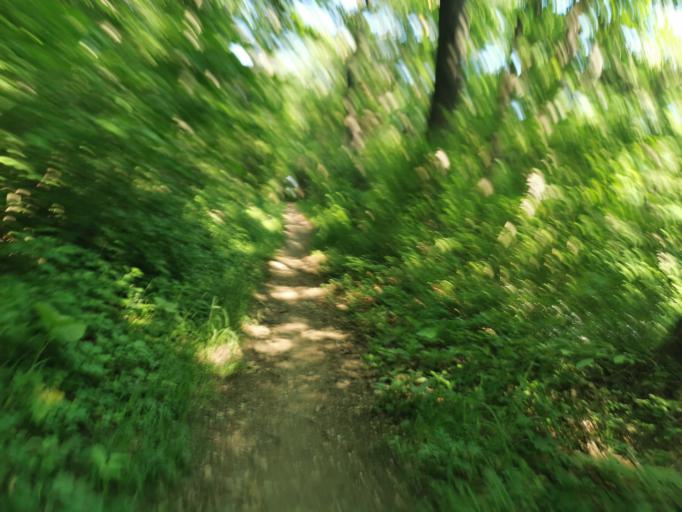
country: CZ
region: South Moravian
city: Knezdub
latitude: 48.8537
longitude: 17.3600
